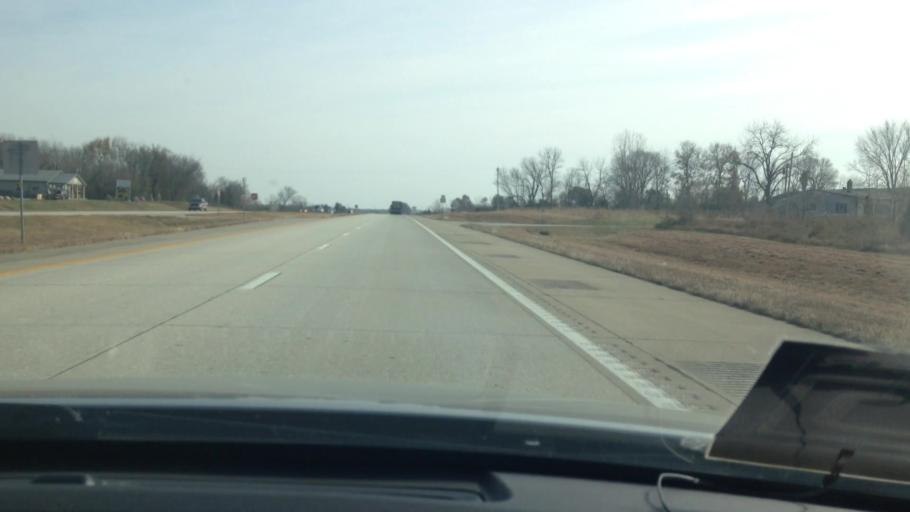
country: US
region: Missouri
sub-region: Henry County
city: Clinton
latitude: 38.4356
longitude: -93.9376
